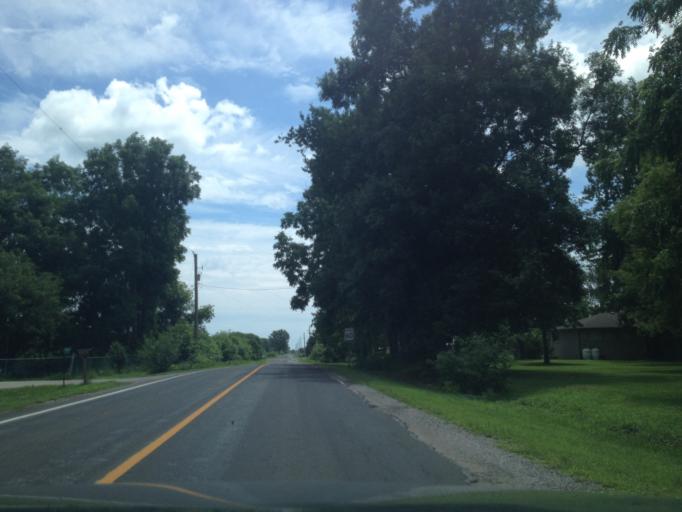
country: CA
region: Ontario
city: Norfolk County
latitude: 42.7960
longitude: -80.3097
